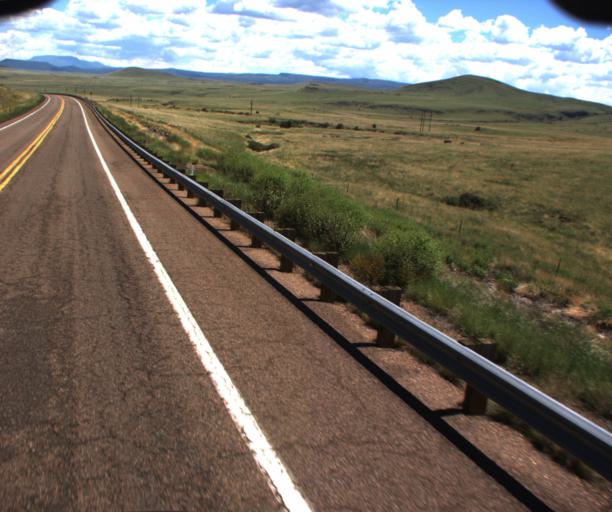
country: US
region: Arizona
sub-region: Apache County
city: Springerville
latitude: 34.2100
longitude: -109.4261
